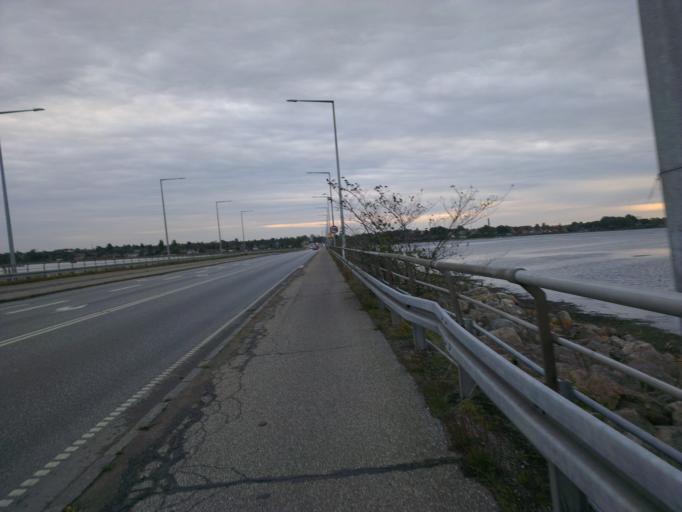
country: DK
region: Capital Region
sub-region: Frederikssund Kommune
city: Frederikssund
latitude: 55.8414
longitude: 12.0334
